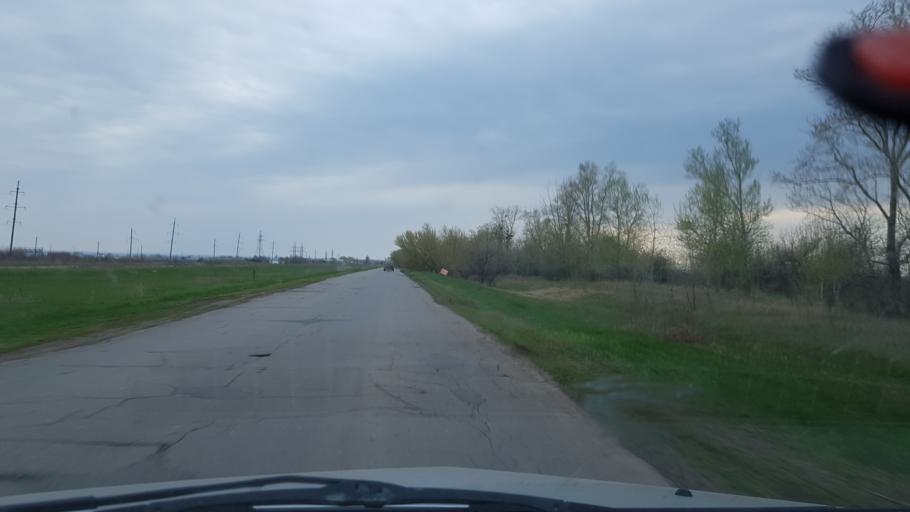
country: RU
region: Samara
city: Khryashchevka
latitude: 53.6710
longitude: 49.1032
